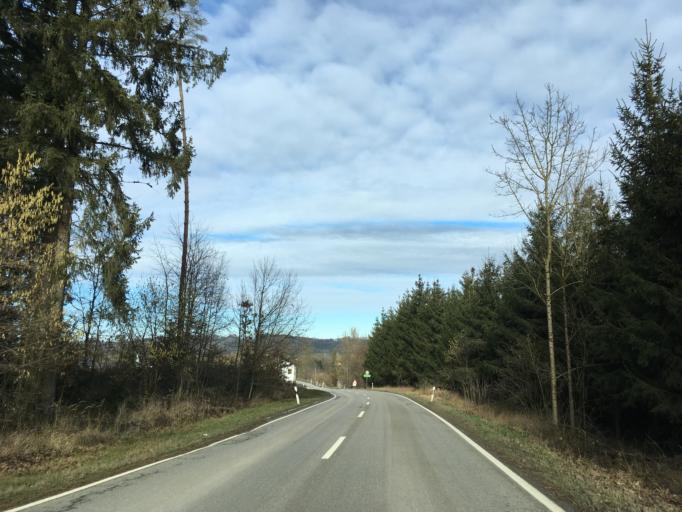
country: DE
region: Bavaria
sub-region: Upper Bavaria
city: Unterreit
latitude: 48.1383
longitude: 12.3092
